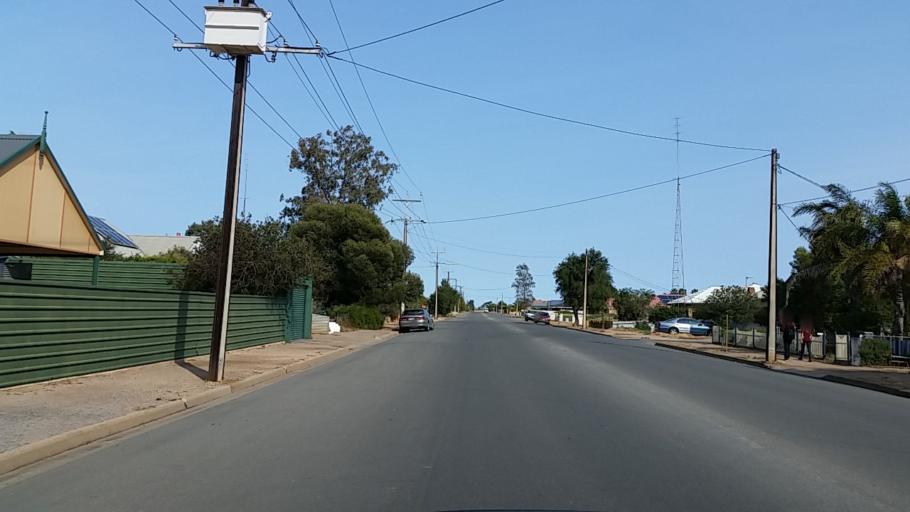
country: AU
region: South Australia
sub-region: Port Pirie City and Dists
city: Port Pirie
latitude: -33.1813
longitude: 137.9950
